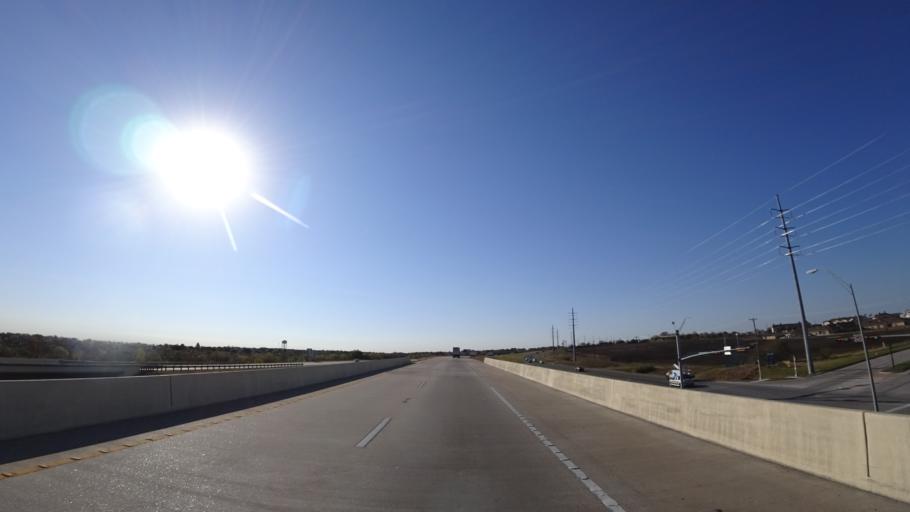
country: US
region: Texas
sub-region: Williamson County
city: Hutto
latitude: 30.5139
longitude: -97.5758
